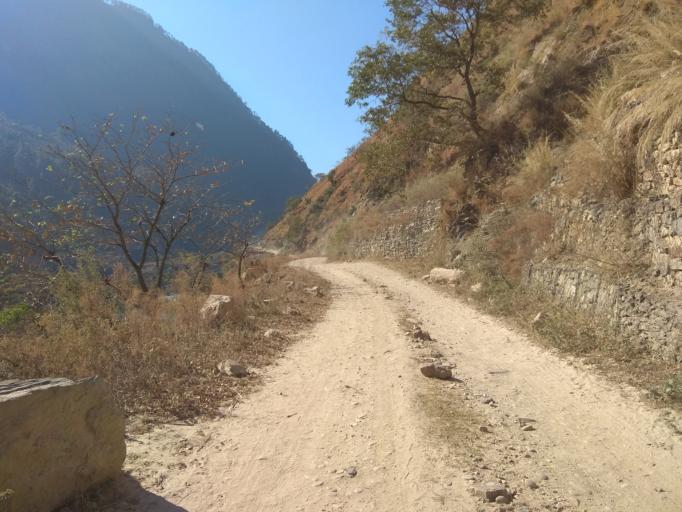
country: NP
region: Mid Western
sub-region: Bheri Zone
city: Dailekh
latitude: 29.2246
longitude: 81.6523
